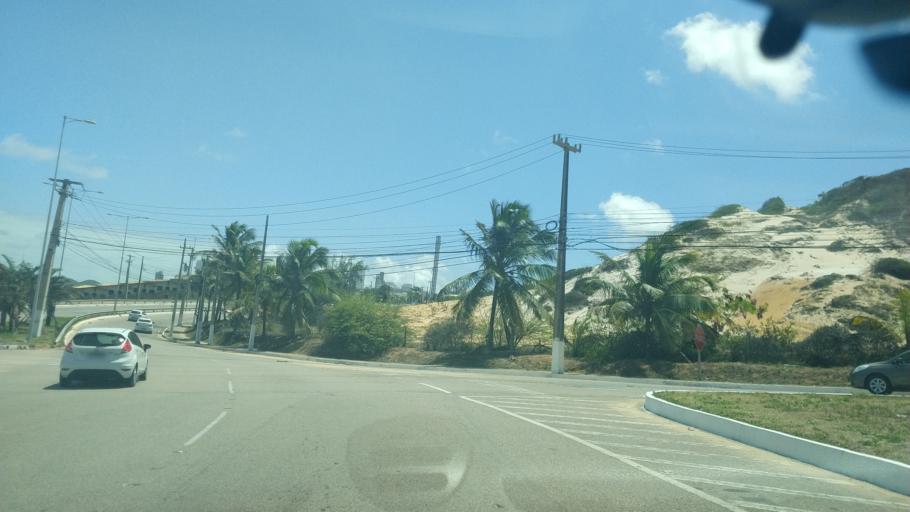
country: BR
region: Rio Grande do Norte
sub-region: Natal
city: Natal
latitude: -5.8634
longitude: -35.1811
